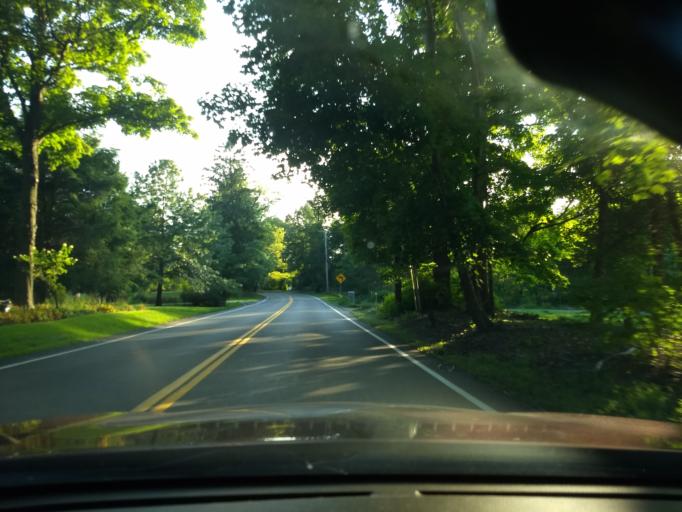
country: US
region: Pennsylvania
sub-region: Allegheny County
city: Gibsonia
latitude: 40.6373
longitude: -79.9538
